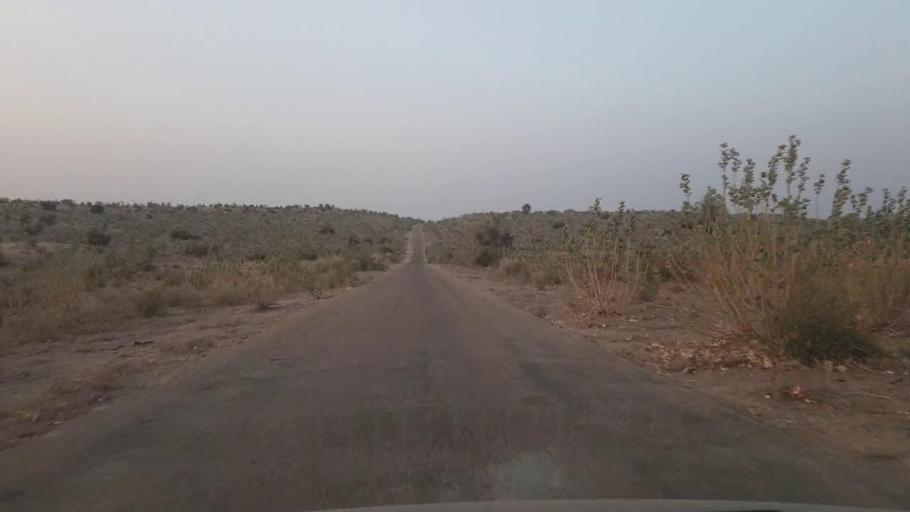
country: PK
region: Sindh
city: Umarkot
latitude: 25.2757
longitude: 70.0770
